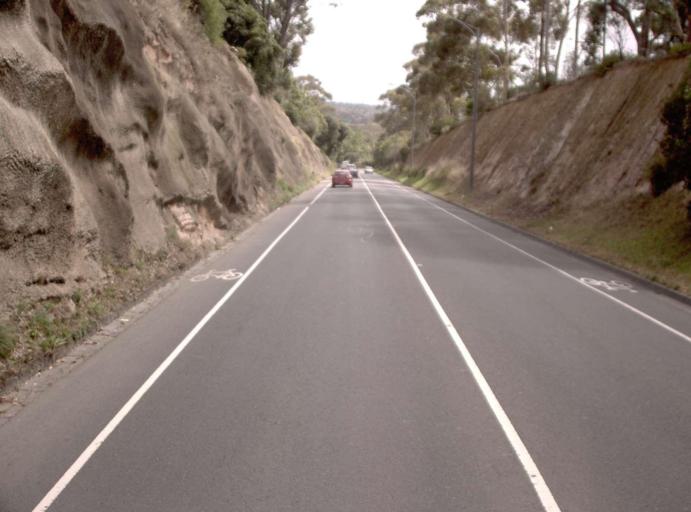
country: AU
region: Victoria
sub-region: Manningham
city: Bulleen
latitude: -37.7691
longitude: 145.0651
